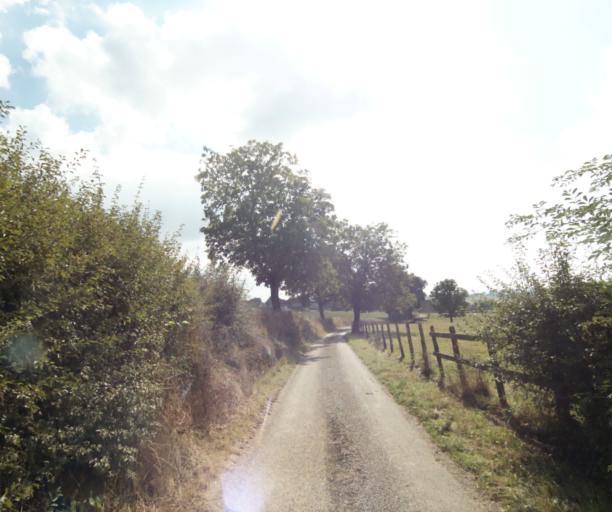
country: FR
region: Bourgogne
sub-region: Departement de Saone-et-Loire
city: Charolles
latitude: 46.3693
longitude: 4.2467
